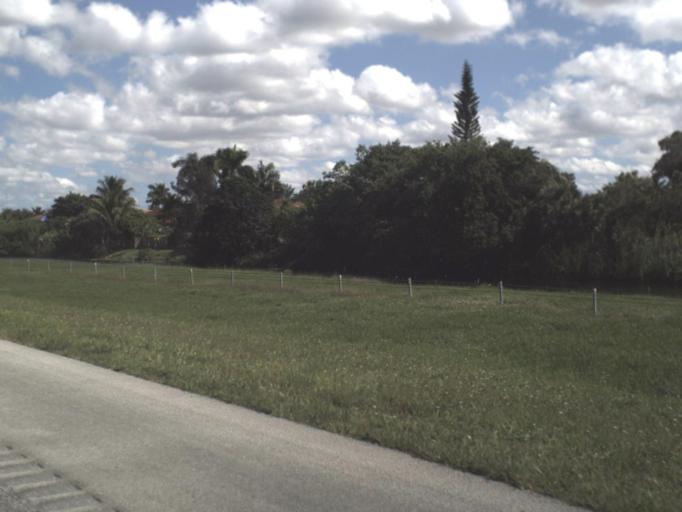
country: US
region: Florida
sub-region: Miami-Dade County
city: Palm Springs North
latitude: 25.9547
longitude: -80.3439
